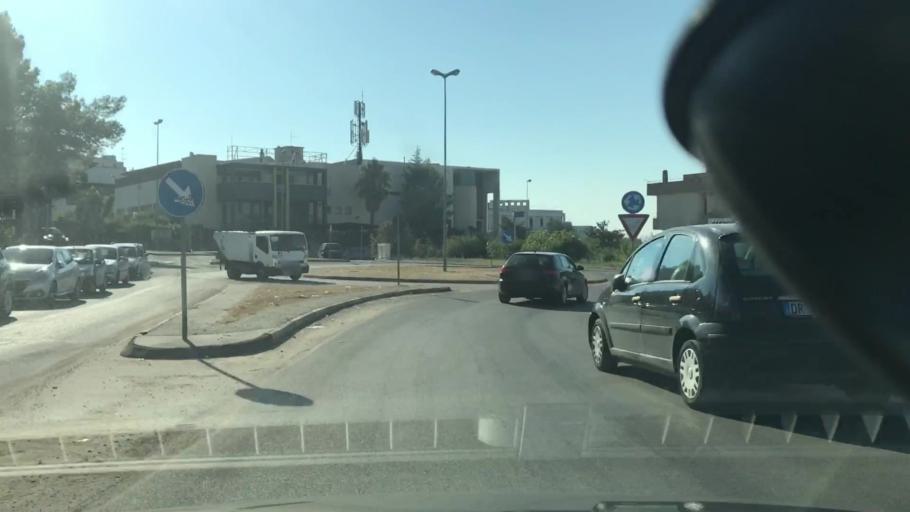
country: IT
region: Basilicate
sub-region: Provincia di Matera
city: Matera
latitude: 40.6754
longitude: 16.5759
